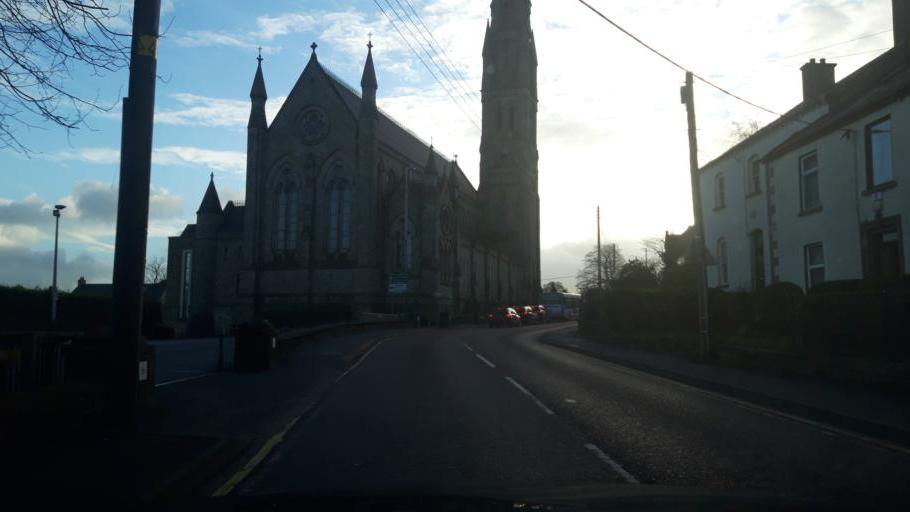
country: GB
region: Northern Ireland
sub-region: Dungannon District
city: Dungannon
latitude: 54.5061
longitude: -6.7636
